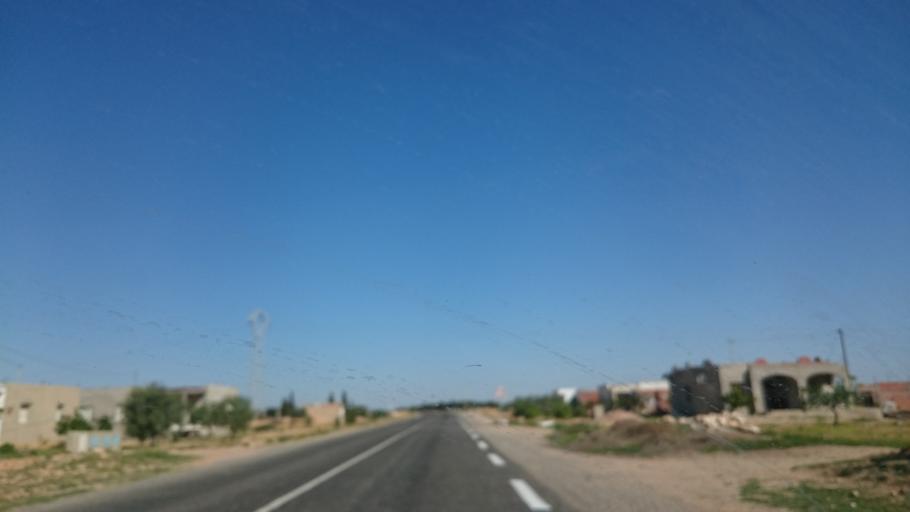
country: TN
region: Safaqis
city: Sfax
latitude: 34.7839
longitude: 10.5020
